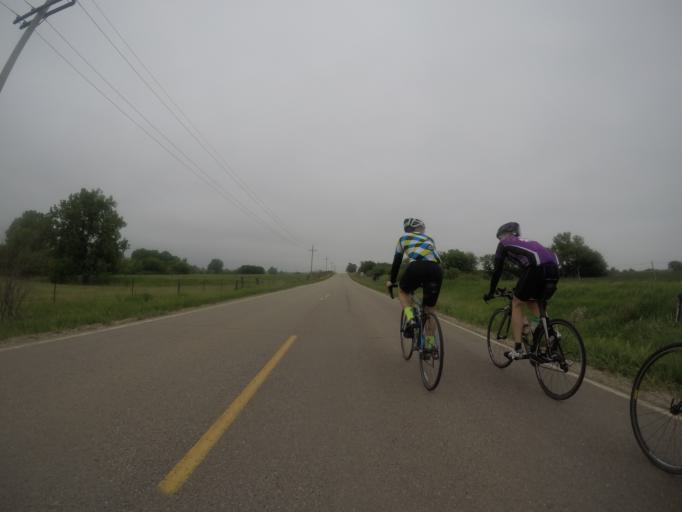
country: US
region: Kansas
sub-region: Pottawatomie County
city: Westmoreland
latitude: 39.5082
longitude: -96.3142
